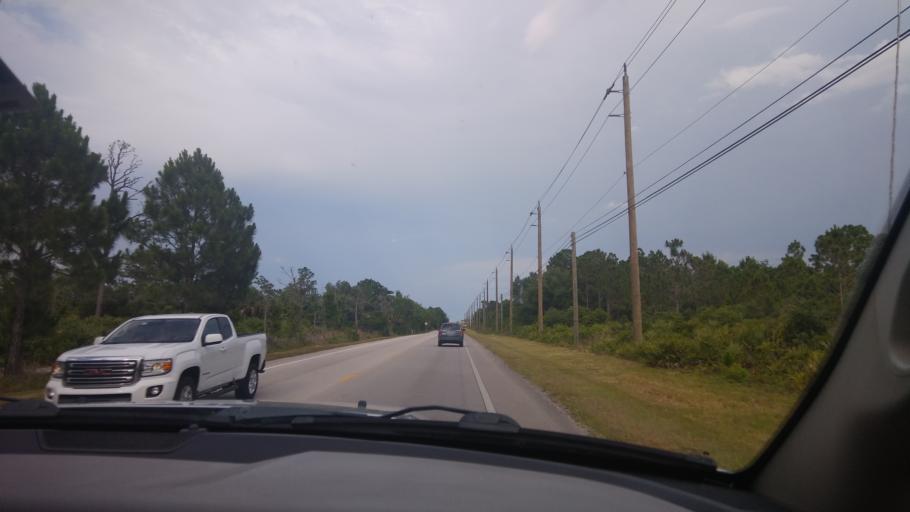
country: US
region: Florida
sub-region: Indian River County
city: Fellsmere
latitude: 27.7676
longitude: -80.5630
